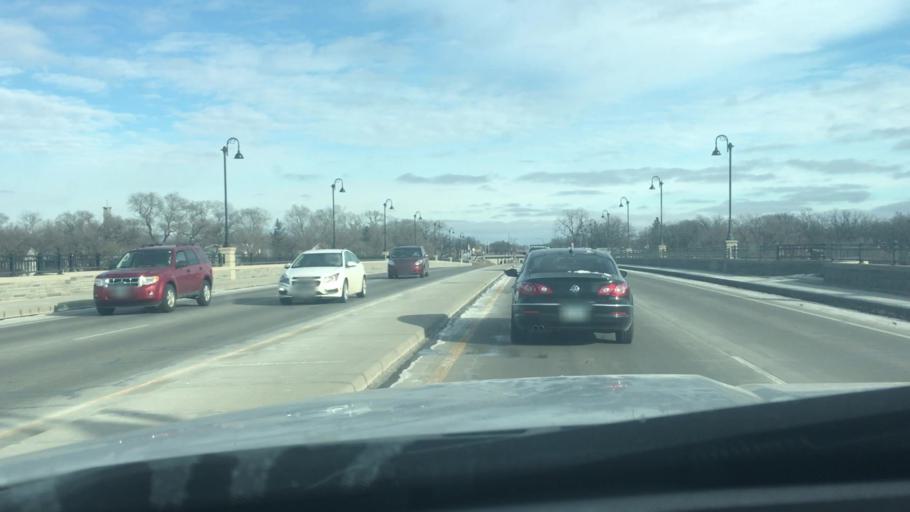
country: US
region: Minnesota
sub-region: Stearns County
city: Saint Cloud
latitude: 45.5608
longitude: -94.1529
